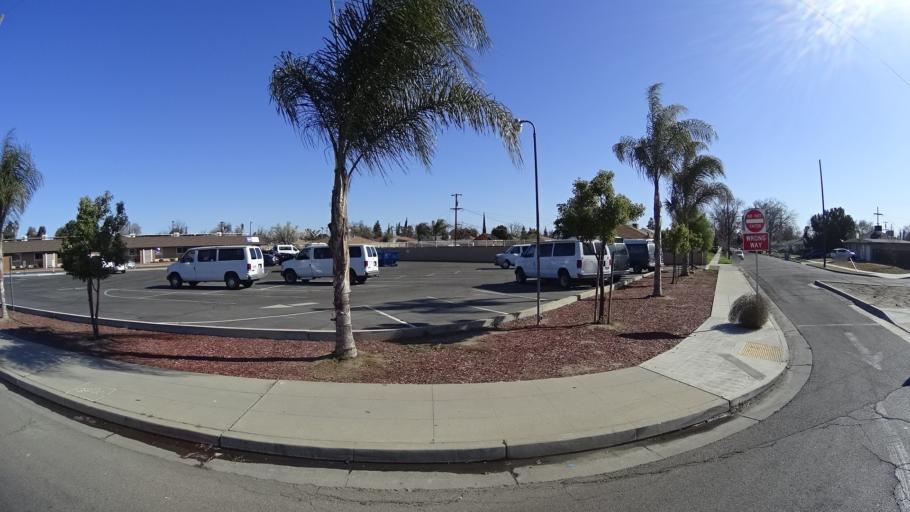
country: US
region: California
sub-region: Fresno County
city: West Park
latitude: 36.7683
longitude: -119.8327
